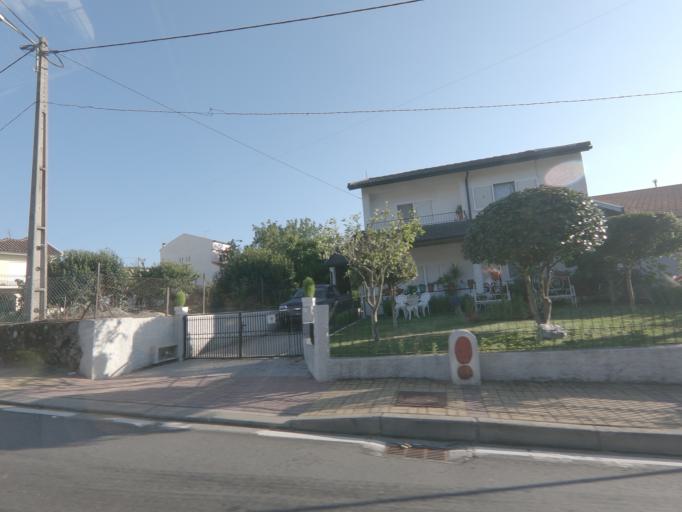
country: PT
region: Vila Real
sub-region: Vila Real
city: Vila Real
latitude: 41.2831
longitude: -7.6980
